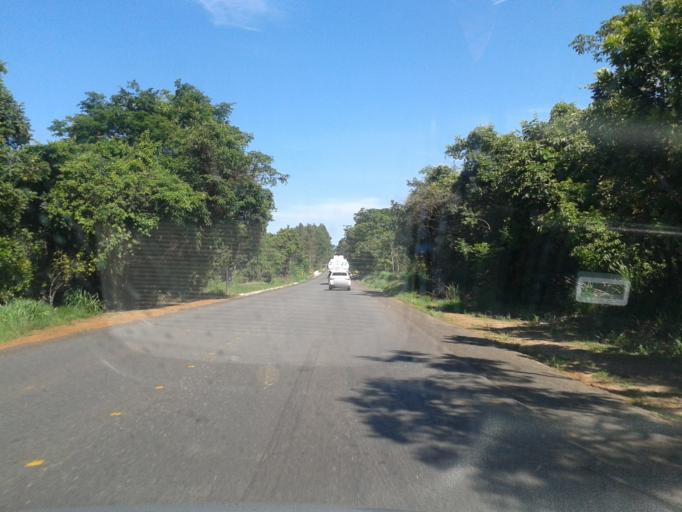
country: BR
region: Goias
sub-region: Bela Vista De Goias
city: Bela Vista de Goias
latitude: -17.0973
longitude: -48.8588
